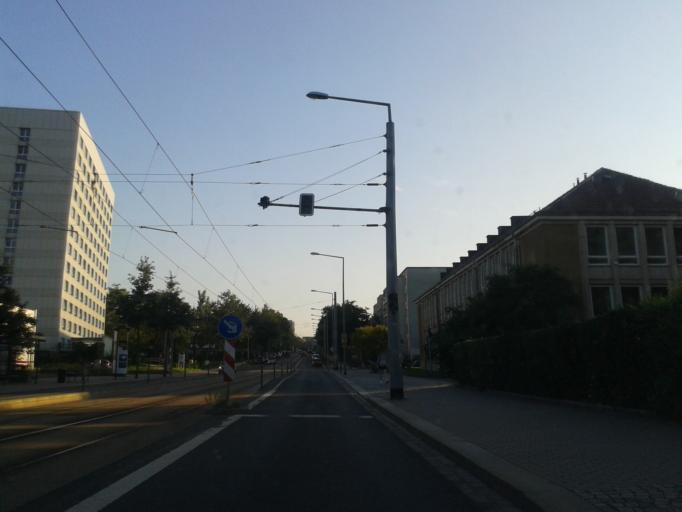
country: DE
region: Saxony
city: Dresden
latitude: 51.0334
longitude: 13.7490
